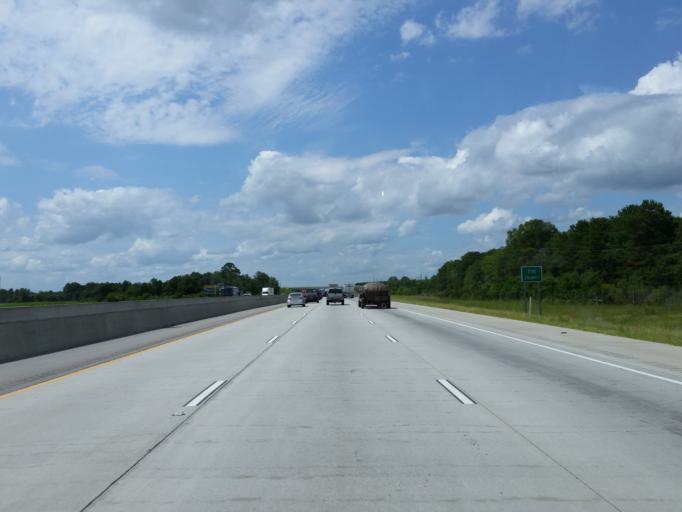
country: US
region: Georgia
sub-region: Tift County
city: Unionville
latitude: 31.3261
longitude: -83.4817
